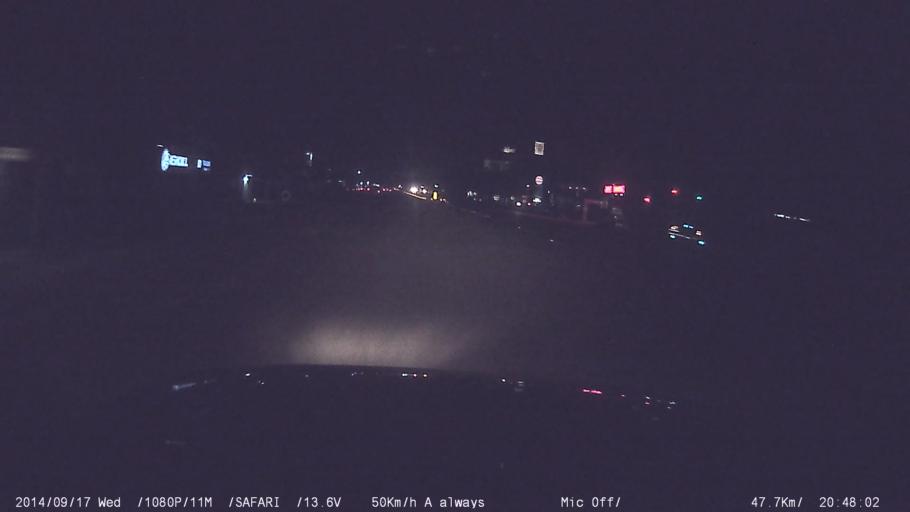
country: IN
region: Kerala
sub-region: Kottayam
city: Kottayam
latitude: 9.5752
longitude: 76.5195
